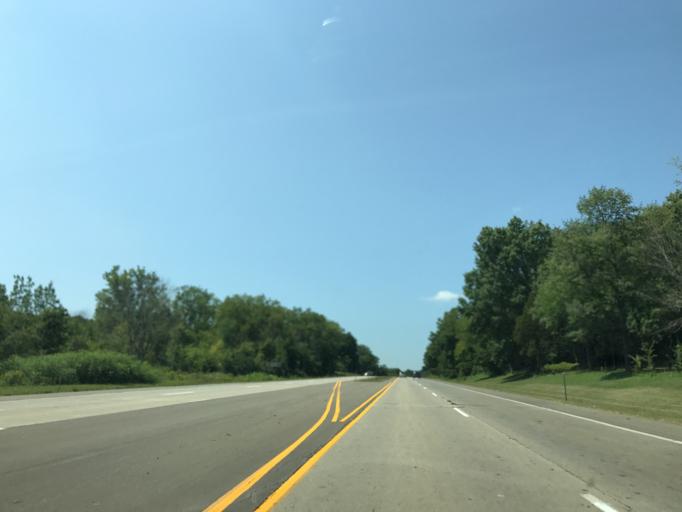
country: US
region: Michigan
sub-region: Berrien County
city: Niles
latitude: 41.8014
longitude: -86.2740
